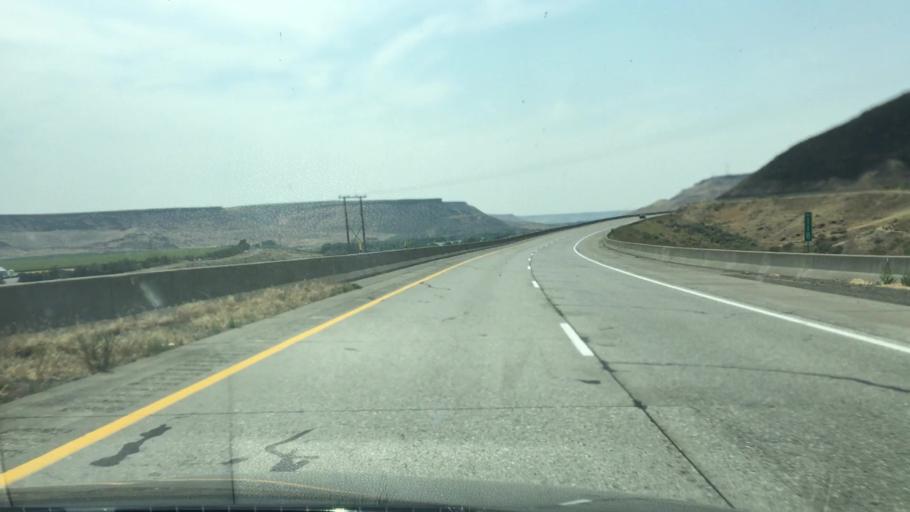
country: US
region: Idaho
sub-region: Elmore County
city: Glenns Ferry
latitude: 42.9581
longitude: -115.3481
